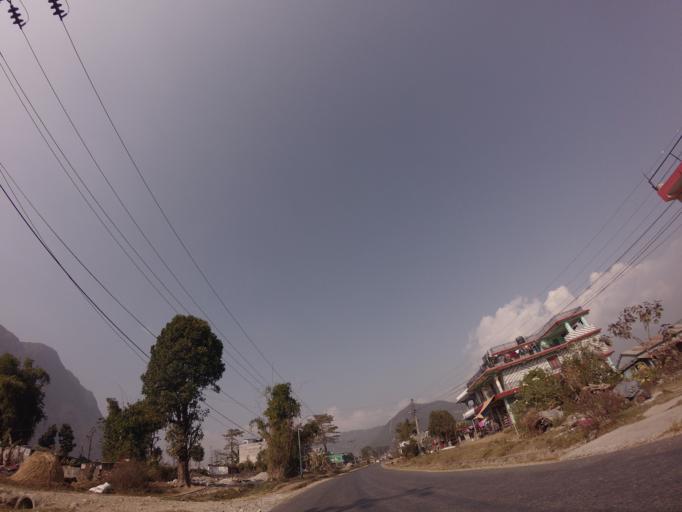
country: NP
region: Western Region
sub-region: Gandaki Zone
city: Pokhara
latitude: 28.2746
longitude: 83.9403
